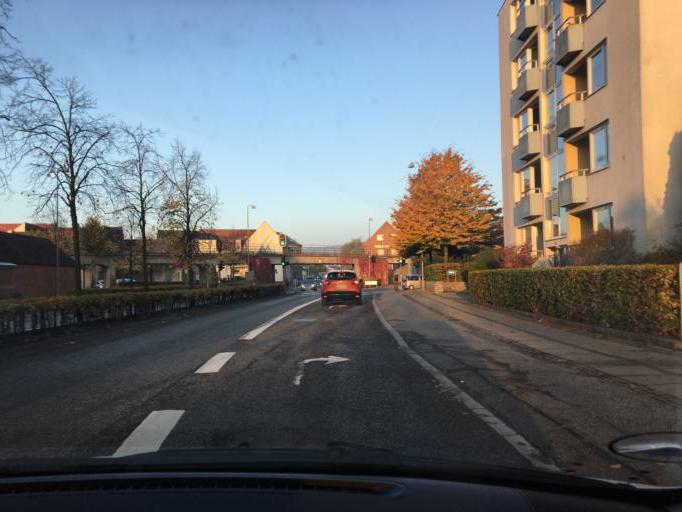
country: DK
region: South Denmark
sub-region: Vejle Kommune
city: Vejle
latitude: 55.7136
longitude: 9.5392
